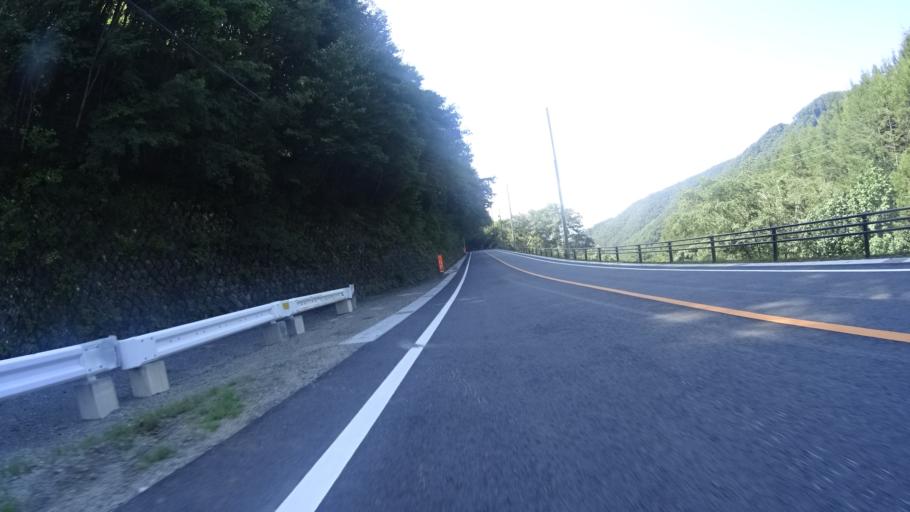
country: JP
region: Yamanashi
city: Enzan
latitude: 35.7741
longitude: 138.8044
